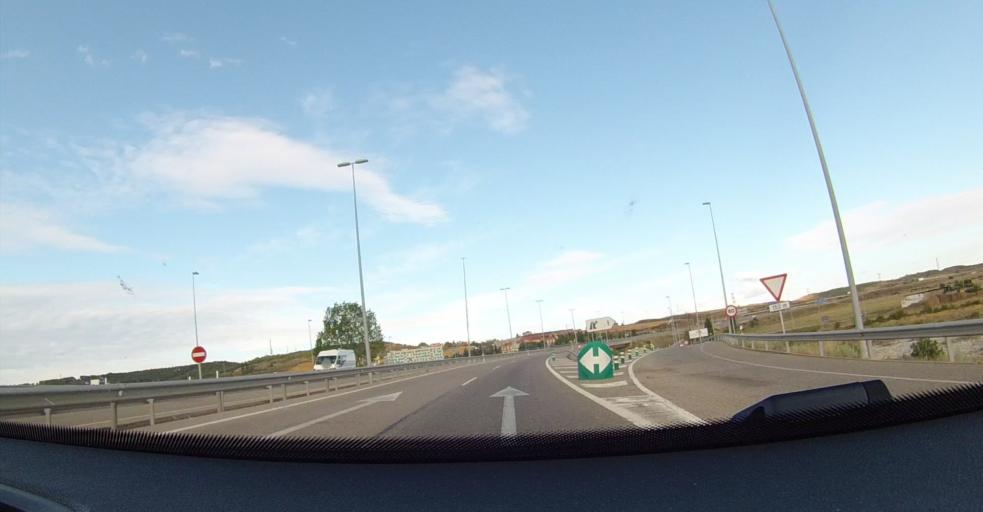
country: ES
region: Castille and Leon
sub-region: Provincia de Leon
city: Leon
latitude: 42.5753
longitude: -5.5554
